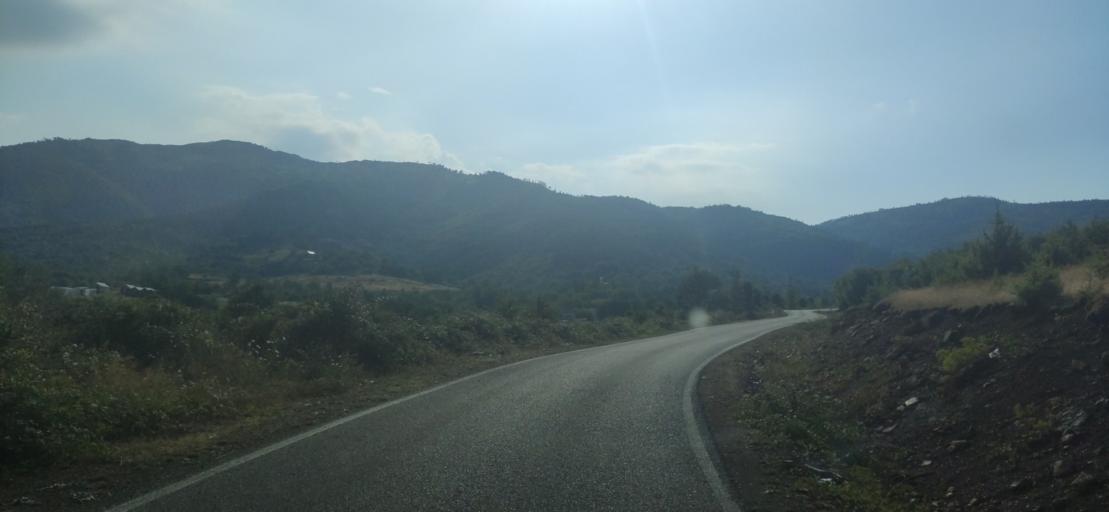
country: AL
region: Shkoder
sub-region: Rrethi i Pukes
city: Iballe
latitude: 42.1823
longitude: 19.9970
